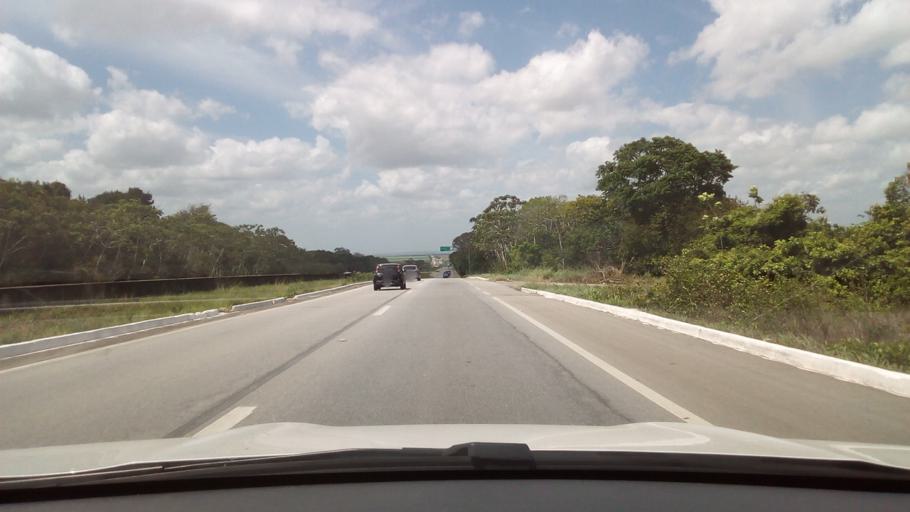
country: BR
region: Paraiba
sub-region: Mamanguape
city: Mamanguape
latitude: -6.9663
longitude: -35.0840
